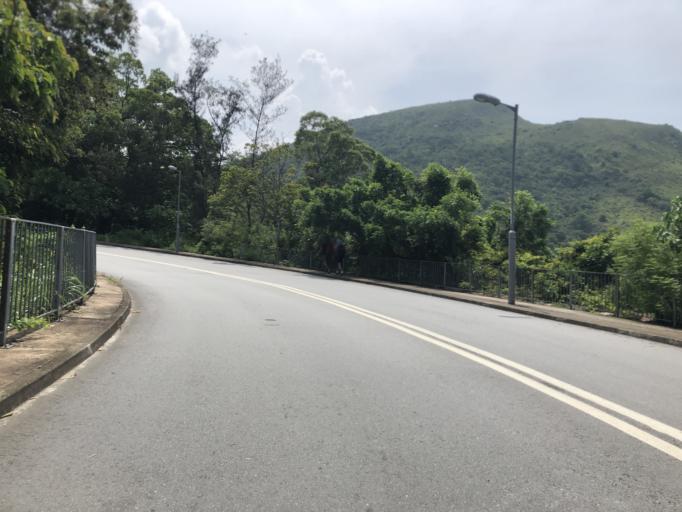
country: CN
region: Guangdong
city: Haishan
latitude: 22.5256
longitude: 114.2105
